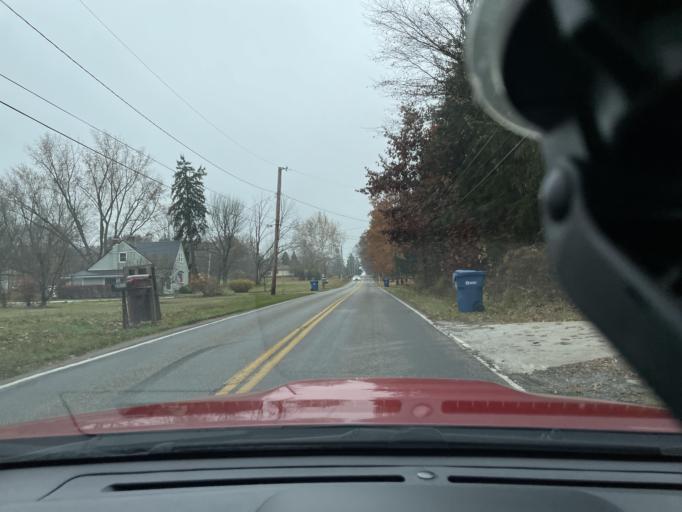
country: US
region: Ohio
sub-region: Trumbull County
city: Mineral Ridge
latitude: 41.1505
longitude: -80.7535
